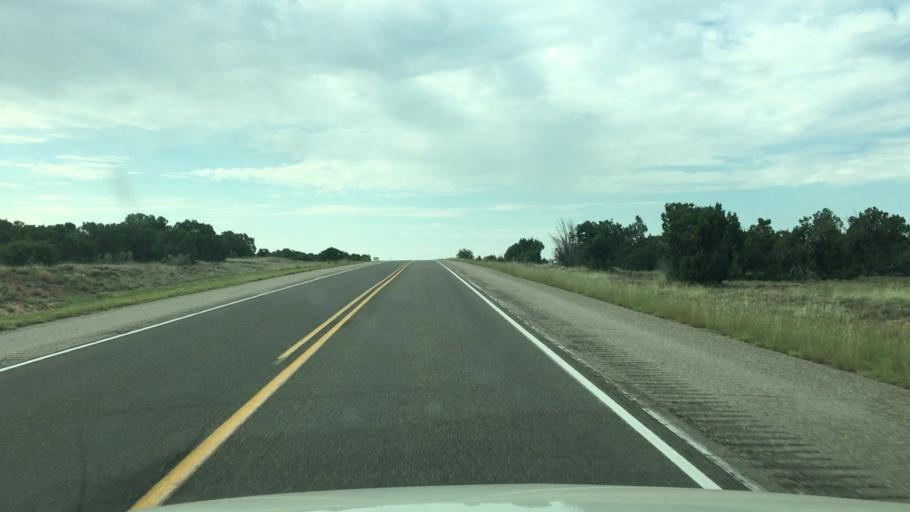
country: US
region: New Mexico
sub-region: Santa Fe County
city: Eldorado at Santa Fe
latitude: 35.2256
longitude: -105.8020
